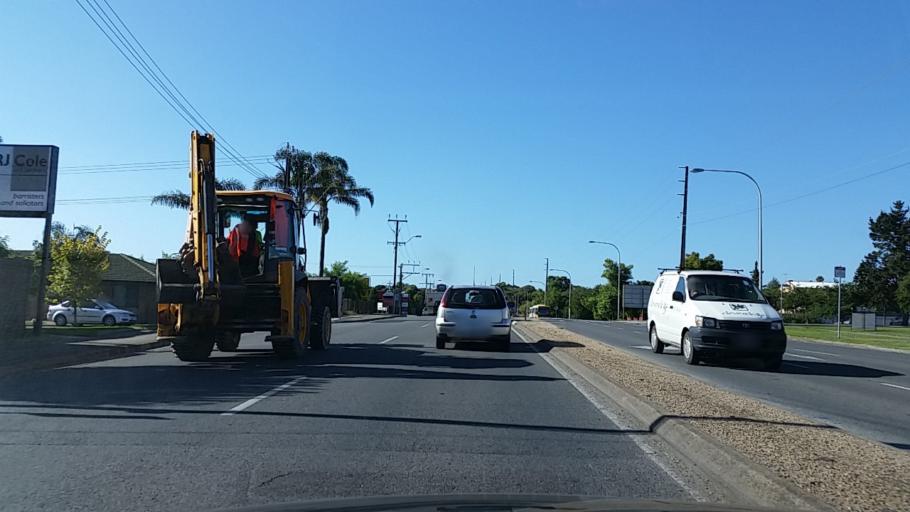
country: AU
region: South Australia
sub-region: Adelaide
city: Port Noarlunga
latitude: -35.1381
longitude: 138.4862
